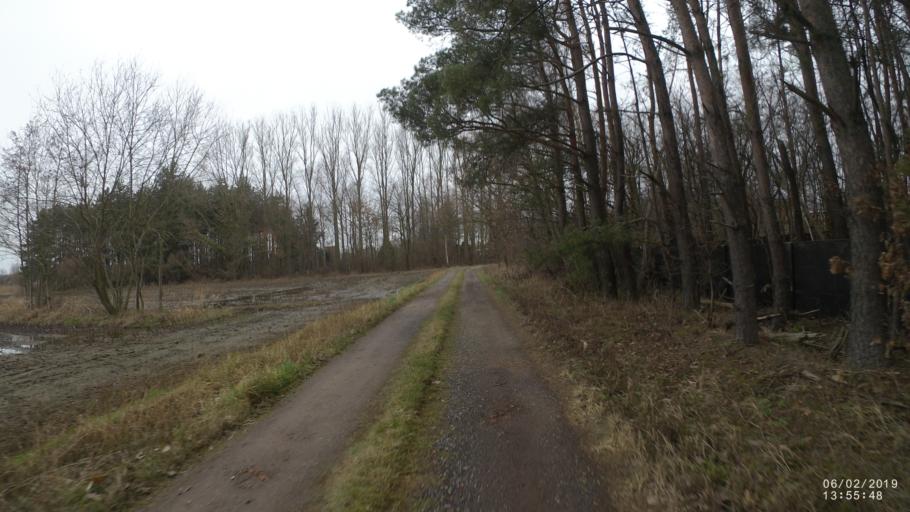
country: BE
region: Flanders
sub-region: Provincie Vlaams-Brabant
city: Begijnendijk
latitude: 51.0359
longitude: 4.7812
